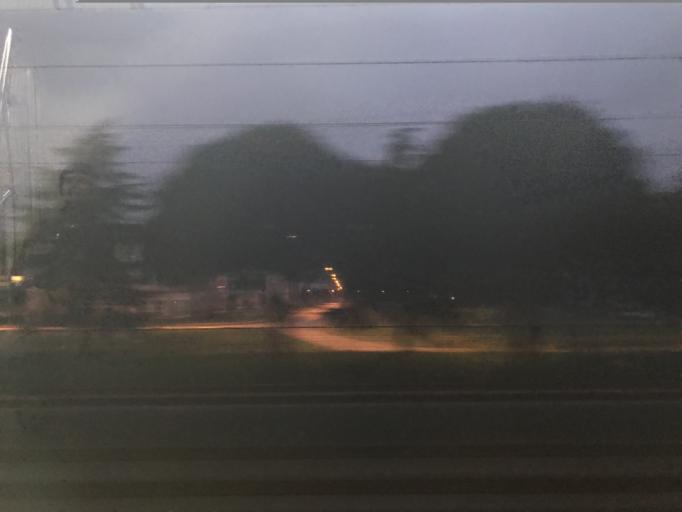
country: TR
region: Kocaeli
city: Darica
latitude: 40.8090
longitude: 29.3562
